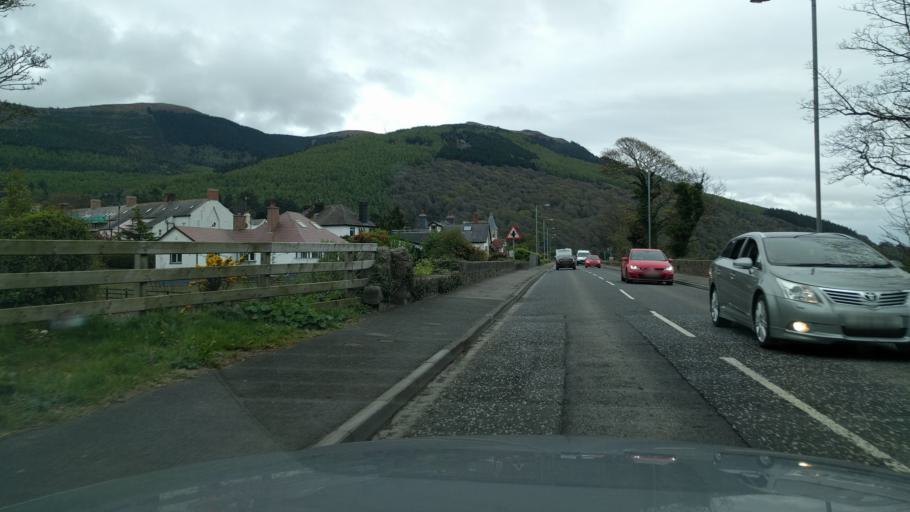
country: GB
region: Northern Ireland
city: Rostrevor
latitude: 54.0982
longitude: -6.1989
